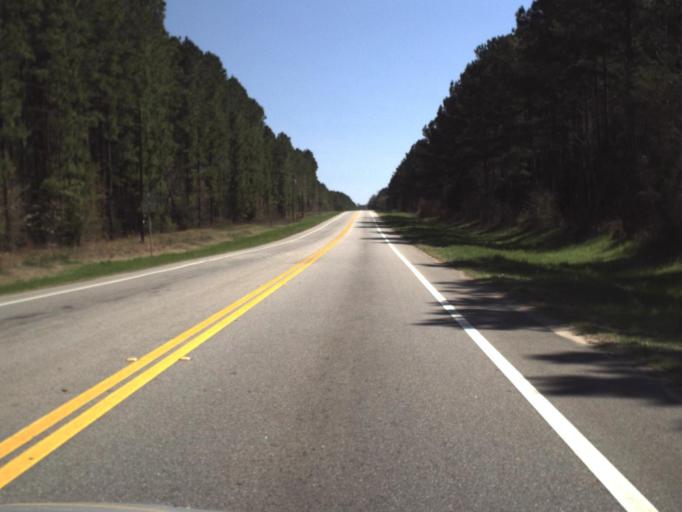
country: US
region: Florida
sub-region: Jackson County
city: Marianna
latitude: 30.8405
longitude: -85.3456
